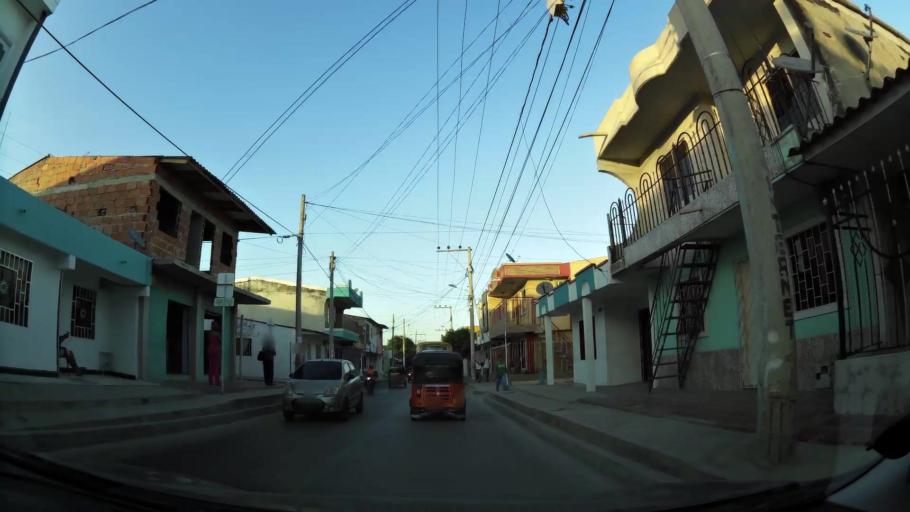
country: CO
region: Atlantico
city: Soledad
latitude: 10.9216
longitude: -74.7878
